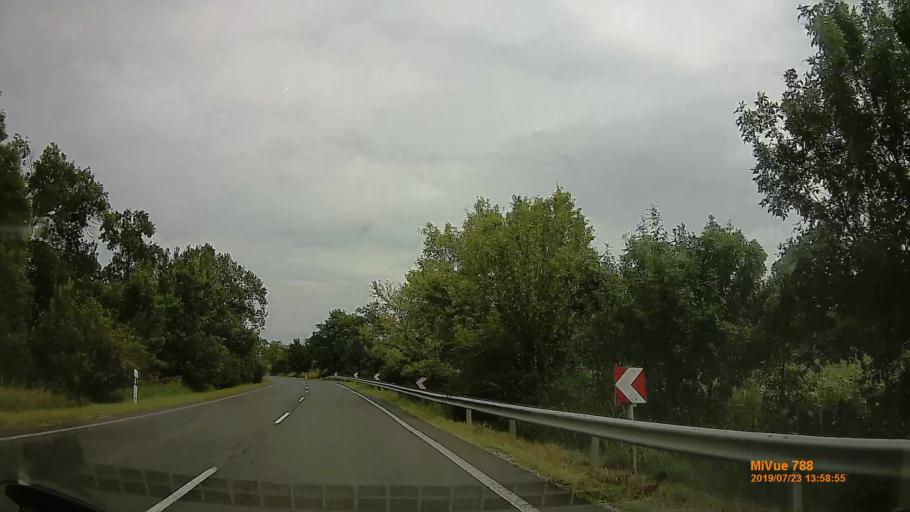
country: HU
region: Szabolcs-Szatmar-Bereg
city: Tiszavasvari
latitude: 47.9256
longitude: 21.2835
